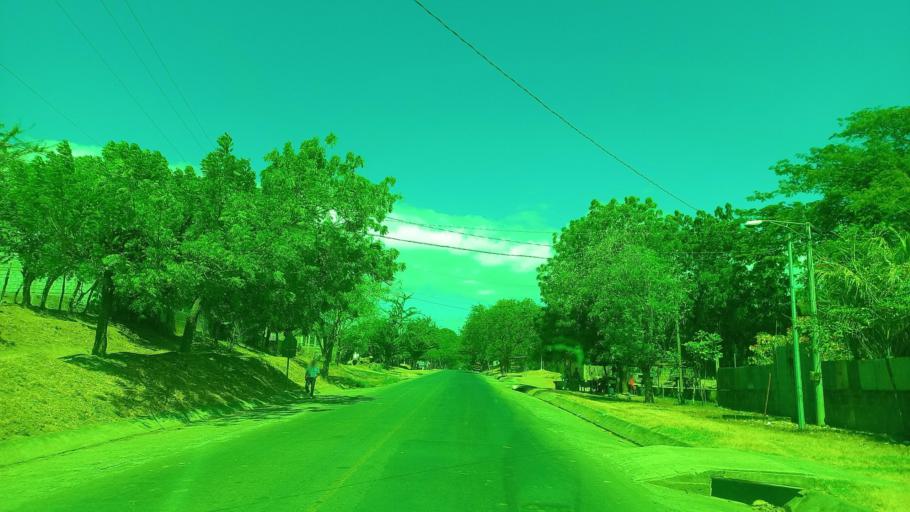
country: NI
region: Managua
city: Ciudad Sandino
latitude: 12.1885
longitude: -86.3368
